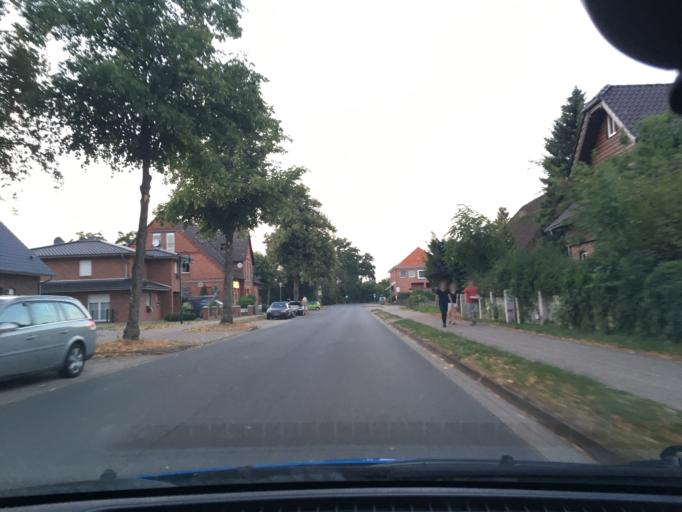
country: DE
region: Lower Saxony
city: Embsen
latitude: 53.1763
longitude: 10.3451
